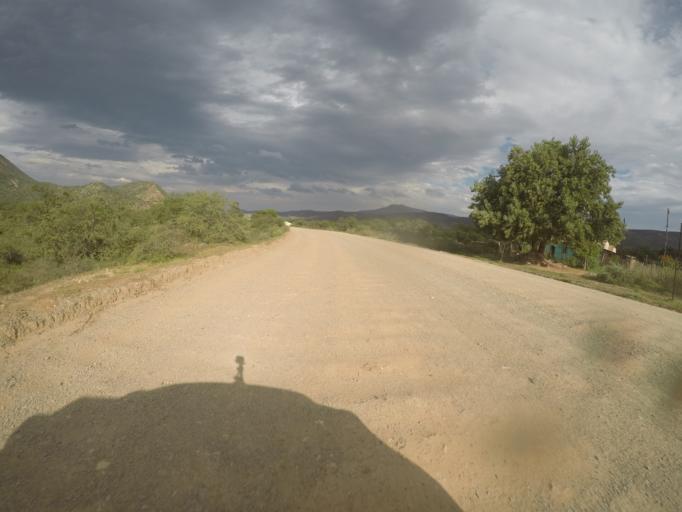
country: ZA
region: Eastern Cape
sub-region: Cacadu District Municipality
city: Kareedouw
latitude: -33.5424
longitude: 23.9782
